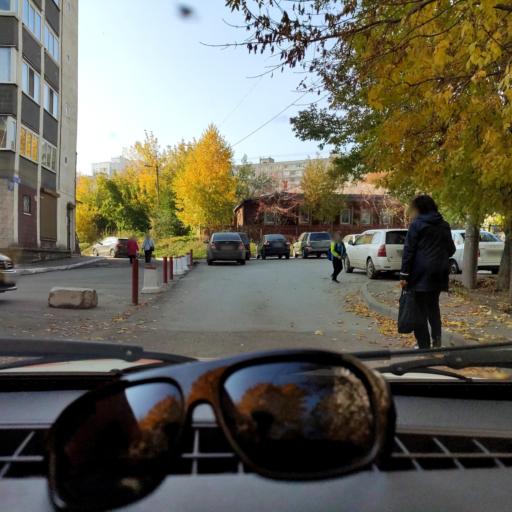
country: RU
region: Bashkortostan
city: Ufa
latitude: 54.7409
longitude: 55.9997
